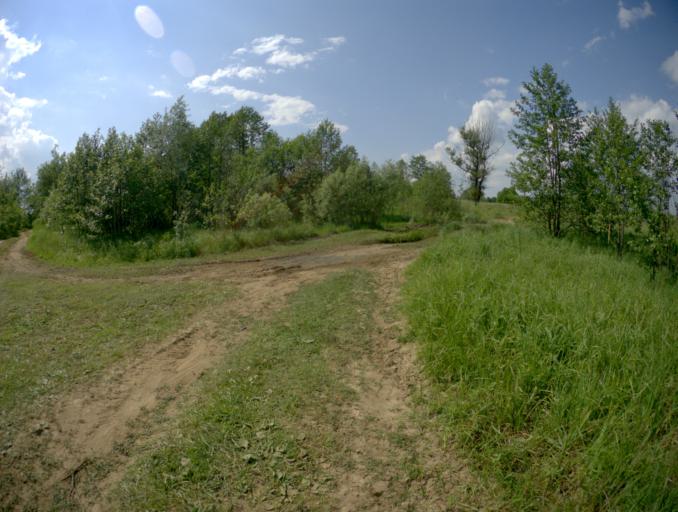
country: RU
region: Vladimir
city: Raduzhnyy
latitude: 56.0395
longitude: 40.3078
